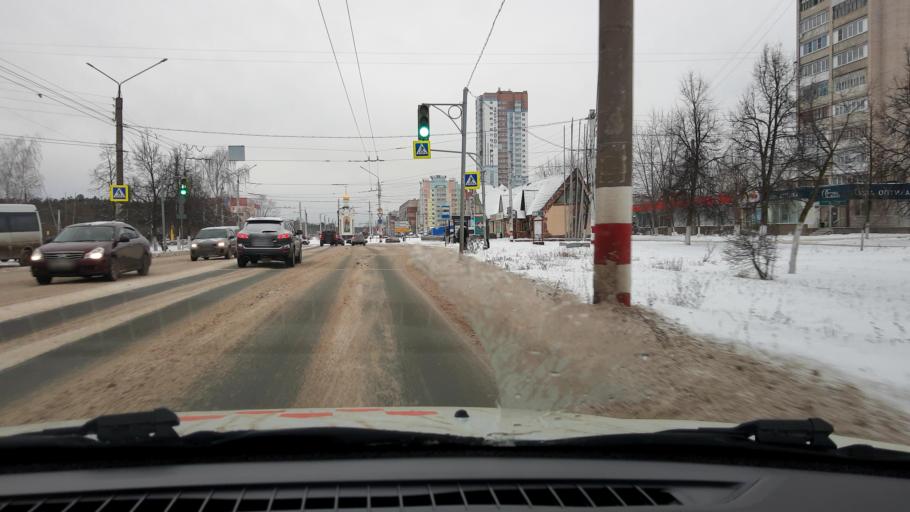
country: RU
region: Nizjnij Novgorod
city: Dzerzhinsk
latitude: 56.2269
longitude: 43.3931
